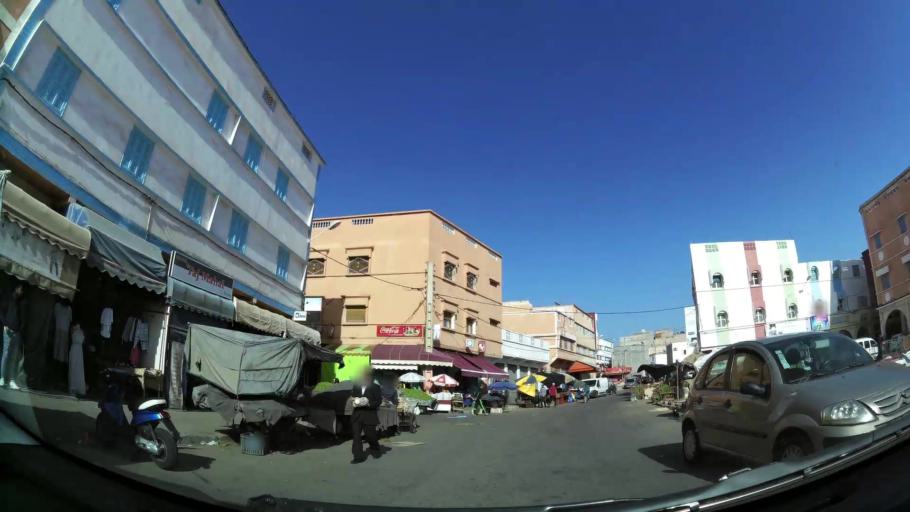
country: MA
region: Souss-Massa-Draa
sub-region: Inezgane-Ait Mellou
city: Inezgane
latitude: 30.3734
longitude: -9.5029
